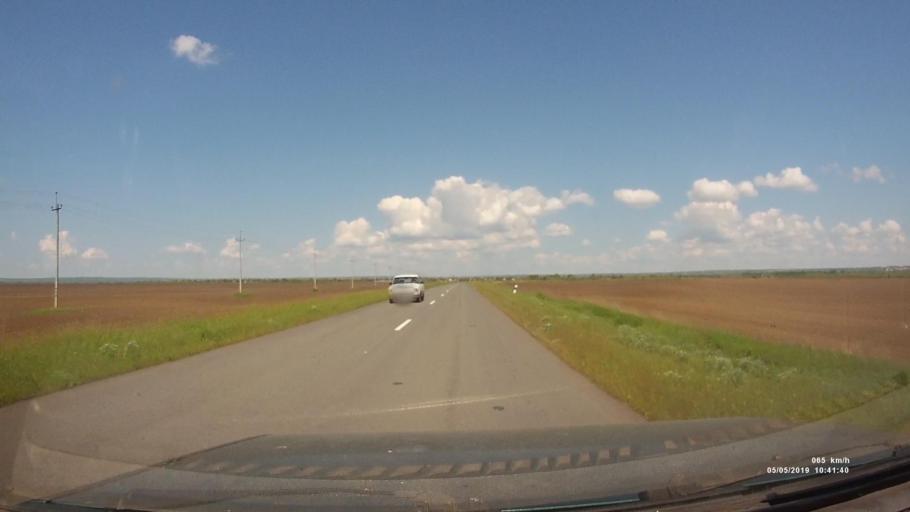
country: RU
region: Rostov
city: Ust'-Donetskiy
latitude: 47.5925
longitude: 40.8403
